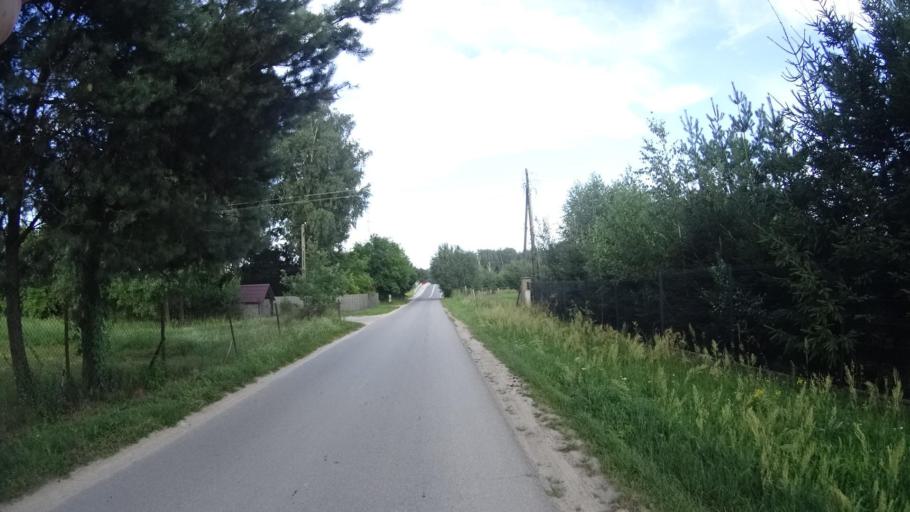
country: PL
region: Masovian Voivodeship
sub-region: Powiat piaseczynski
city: Tarczyn
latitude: 51.9663
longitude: 20.8556
